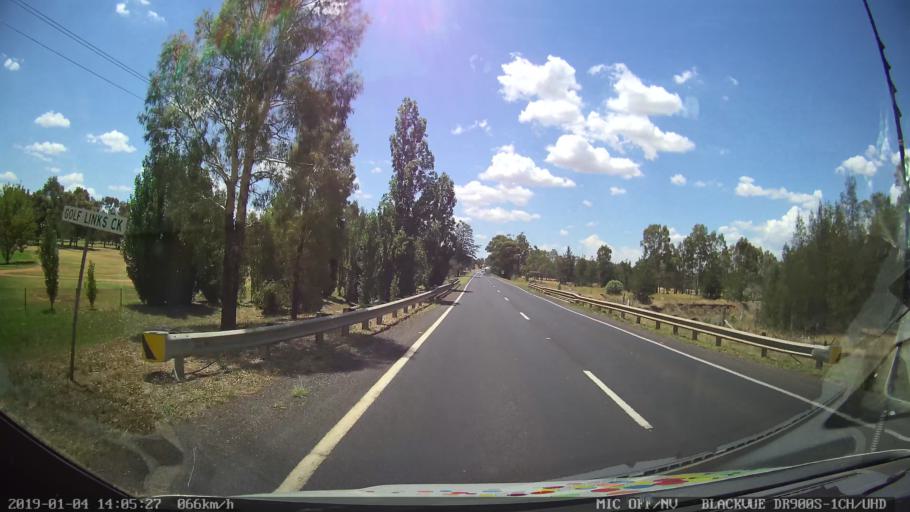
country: AU
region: New South Wales
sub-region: Dubbo Municipality
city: Dubbo
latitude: -32.2623
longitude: 148.5854
